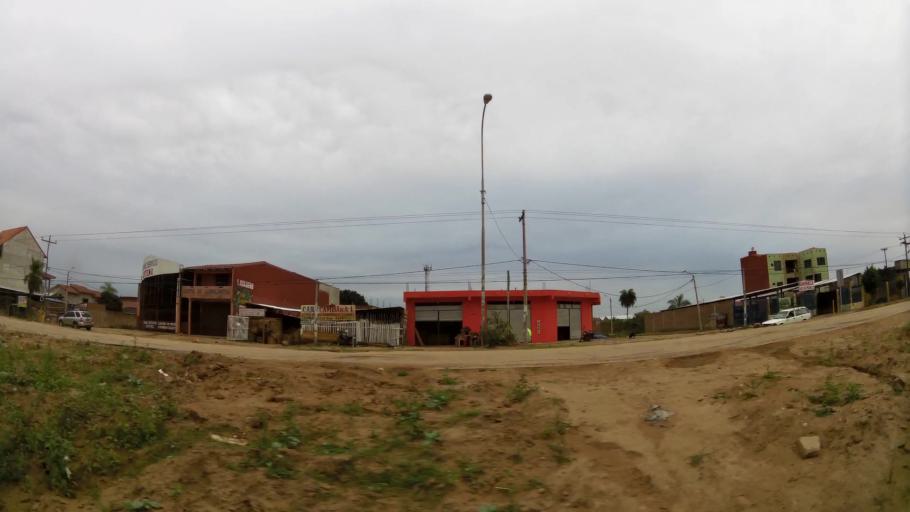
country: BO
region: Santa Cruz
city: Santa Cruz de la Sierra
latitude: -17.8534
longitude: -63.1841
